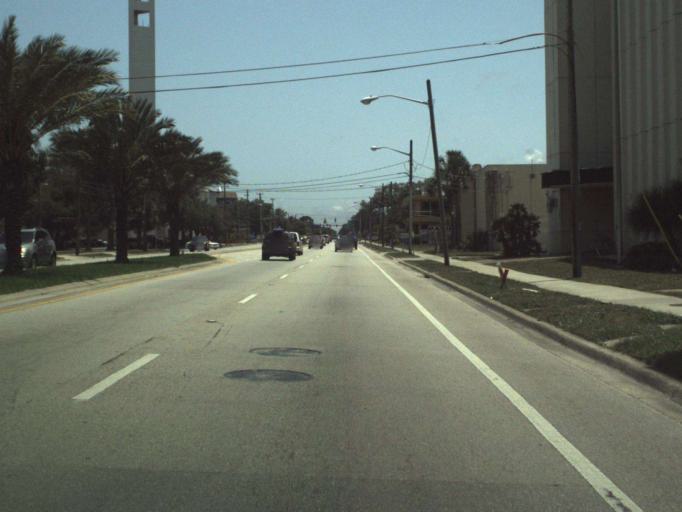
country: US
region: Florida
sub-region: Volusia County
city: Daytona Beach
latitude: 29.2150
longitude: -81.0251
